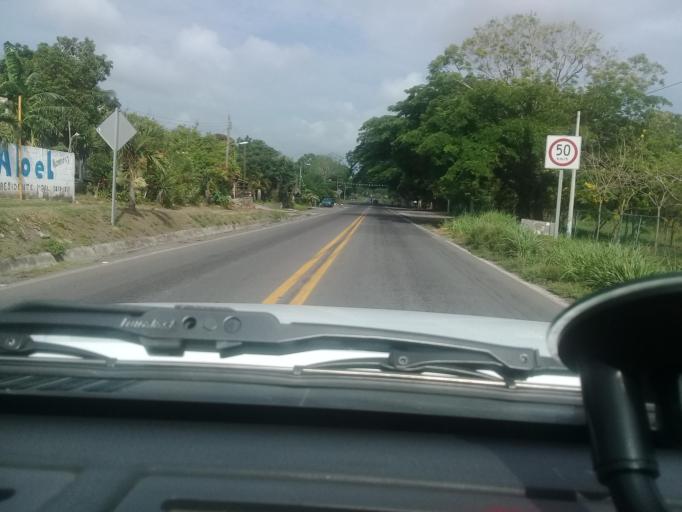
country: MX
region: Veracruz
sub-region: Paso de Ovejas
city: Tolome
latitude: 19.2656
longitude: -96.3761
